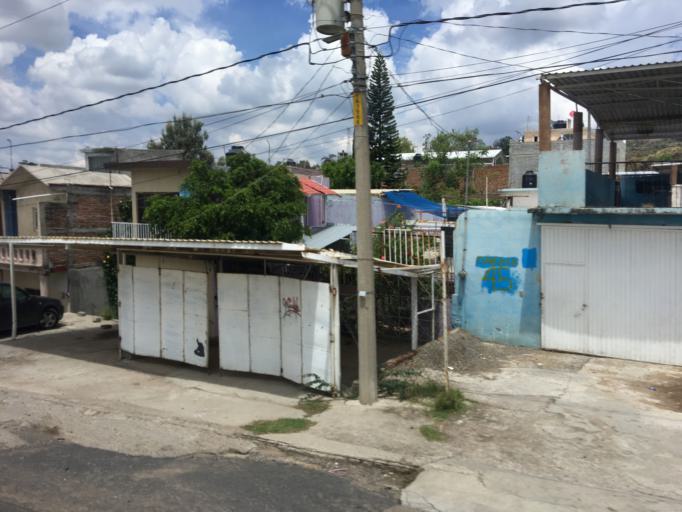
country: MX
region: Guanajuato
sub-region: Irapuato
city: Ex-Hacienda del Copal
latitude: 20.7305
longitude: -101.3432
